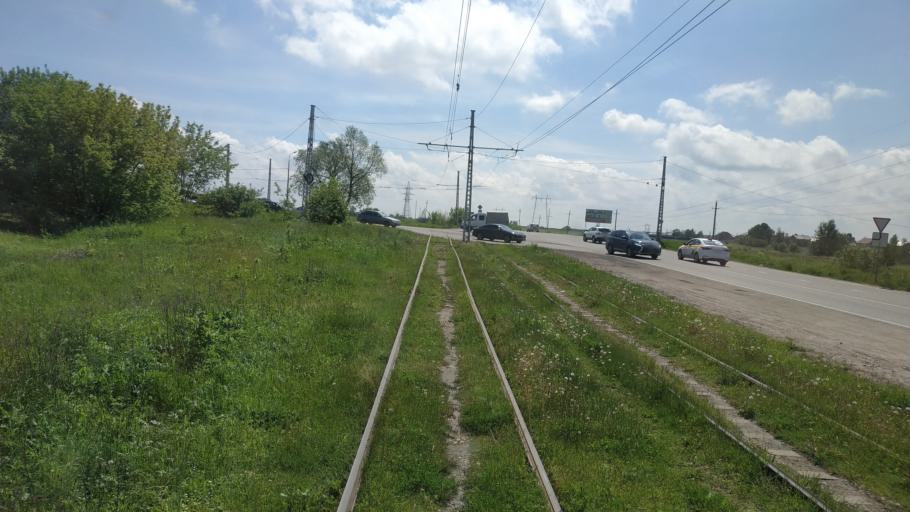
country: RU
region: Moskovskaya
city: Sychevo
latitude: 55.0601
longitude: 38.7270
